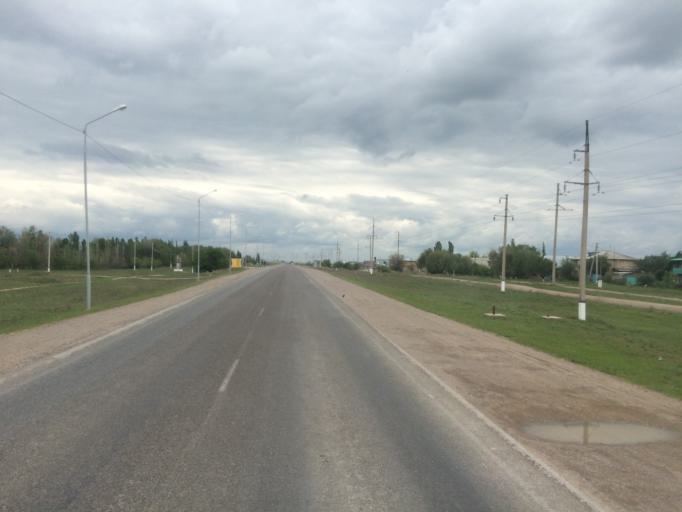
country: KG
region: Chuy
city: Sokuluk
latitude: 43.2497
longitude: 74.2903
